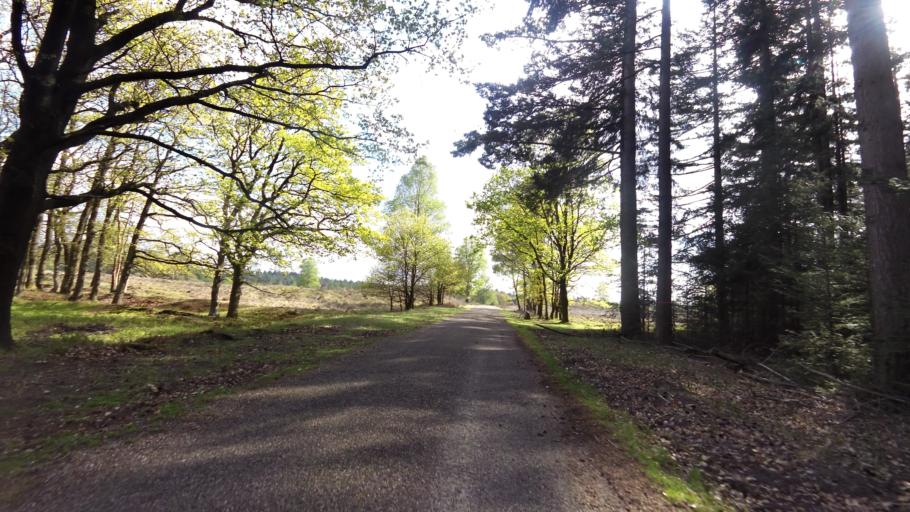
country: NL
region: Gelderland
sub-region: Gemeente Apeldoorn
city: Loenen
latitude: 52.0932
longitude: 5.9722
